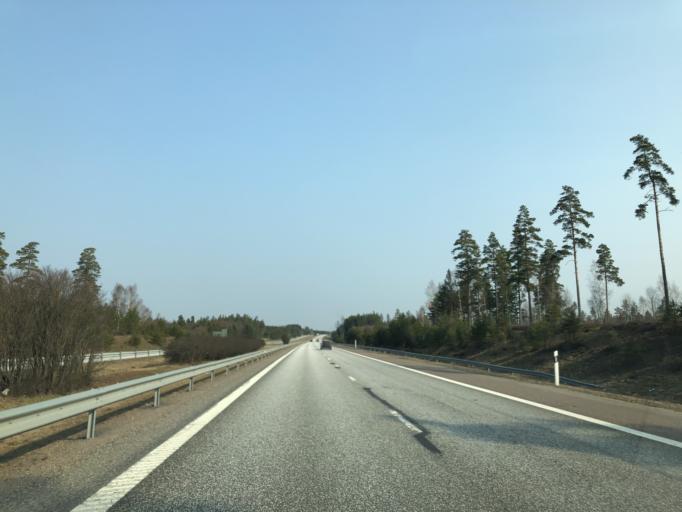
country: SE
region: Joenkoeping
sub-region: Vaggeryds Kommun
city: Skillingaryd
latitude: 57.4649
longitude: 14.0982
